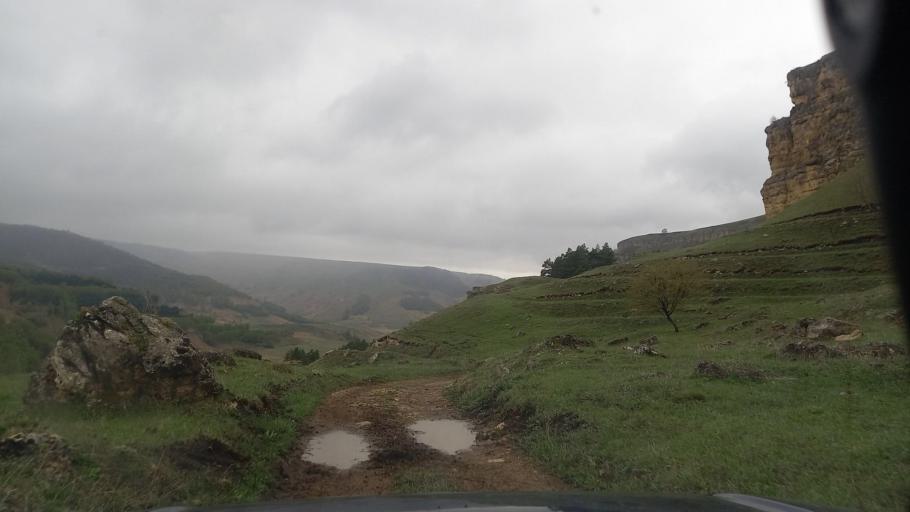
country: RU
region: Stavropol'skiy
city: Nezhinskiy
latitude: 43.8490
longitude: 42.6354
